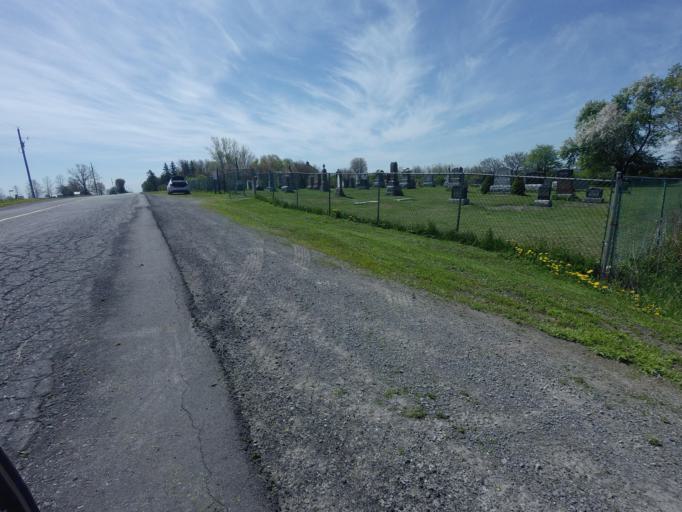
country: CA
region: Ontario
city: Arnprior
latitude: 45.3831
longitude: -76.1306
